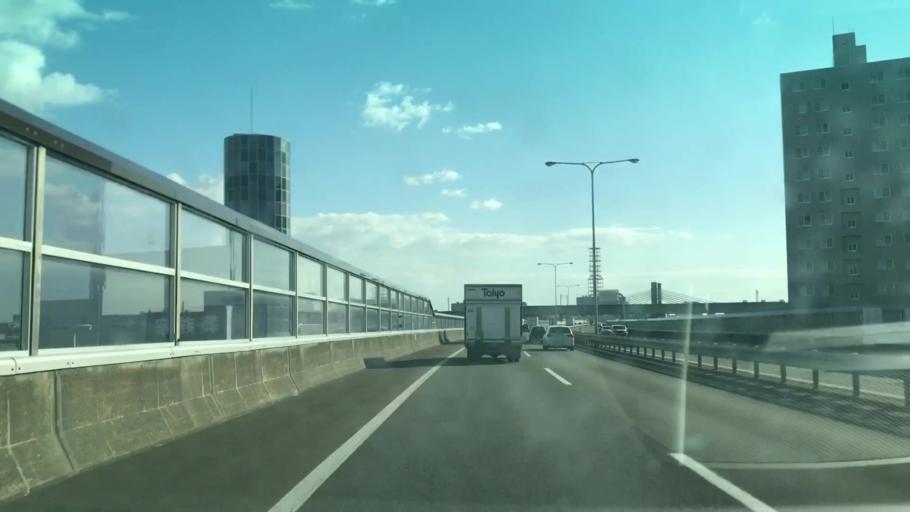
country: JP
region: Hokkaido
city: Sapporo
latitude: 43.1025
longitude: 141.3213
